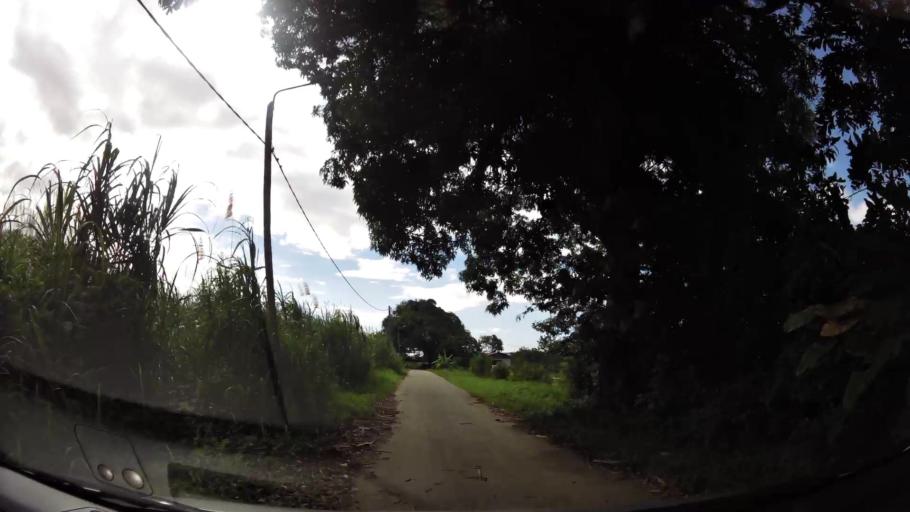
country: SR
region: Paramaribo
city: Paramaribo
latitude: 5.8519
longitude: -55.1605
